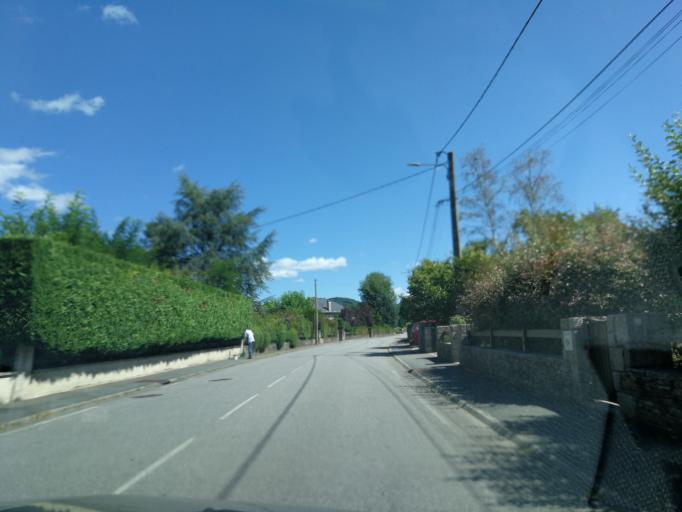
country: FR
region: Limousin
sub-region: Departement de la Correze
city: Argentat
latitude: 45.0904
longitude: 1.9297
